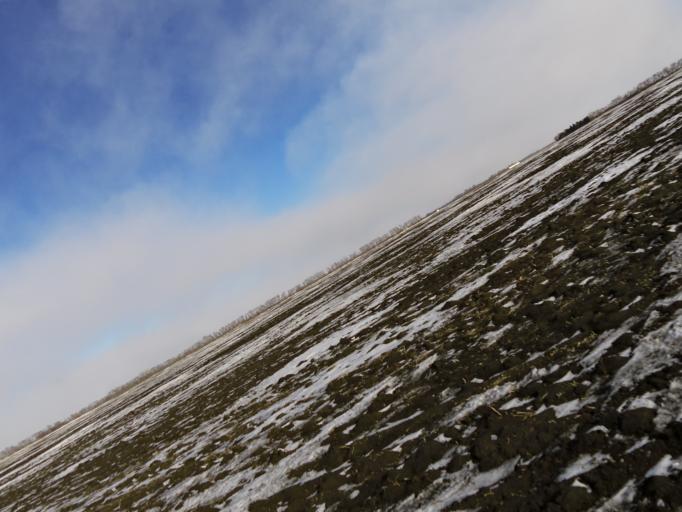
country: US
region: North Dakota
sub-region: Walsh County
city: Grafton
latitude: 48.3989
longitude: -97.2072
